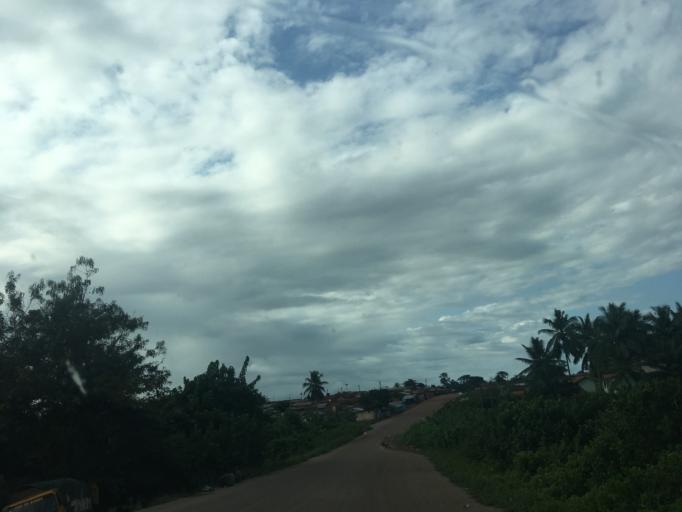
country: GH
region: Western
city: Wassa-Akropong
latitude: 6.0006
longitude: -2.4107
